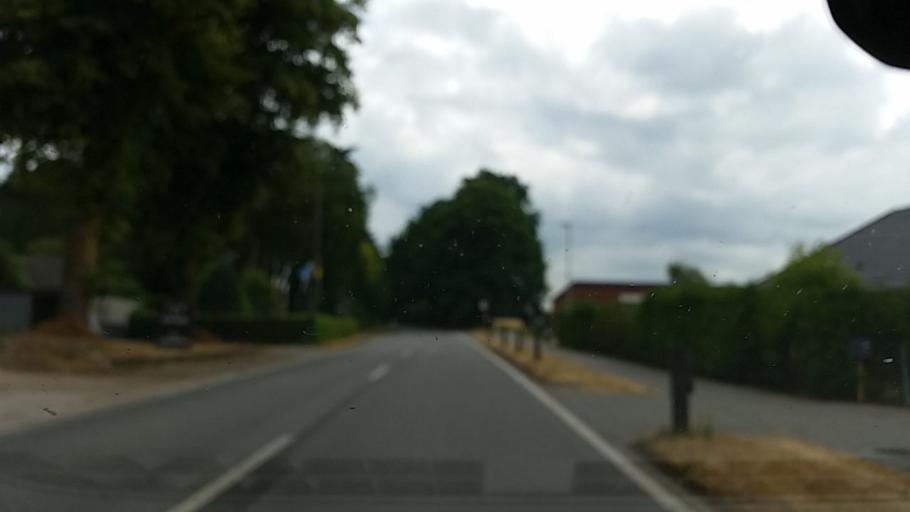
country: DE
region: Schleswig-Holstein
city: Sulfeld
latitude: 53.7666
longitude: 10.2258
